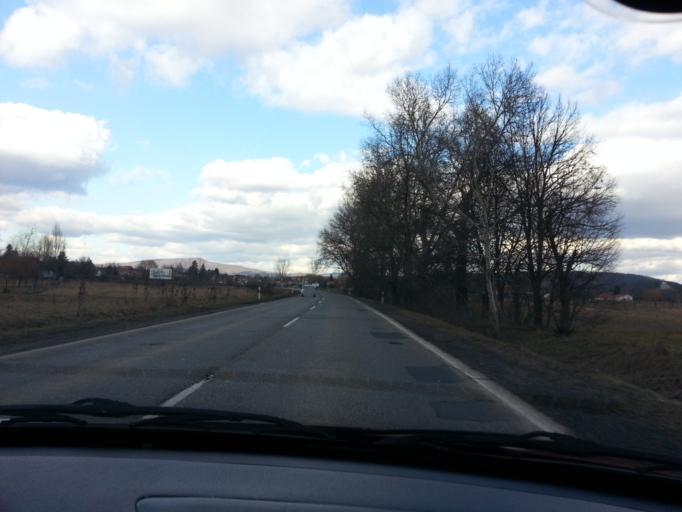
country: HU
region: Nograd
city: Batonyterenye
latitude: 48.0010
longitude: 19.8226
